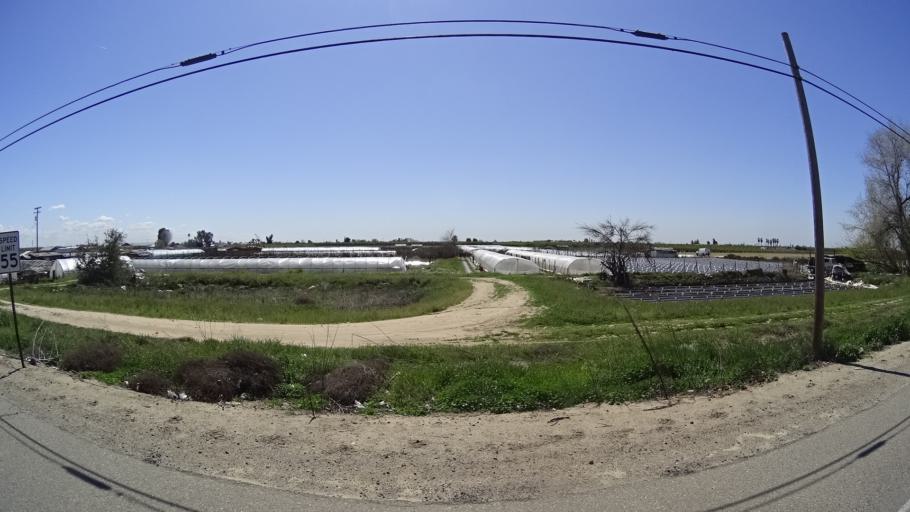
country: US
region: California
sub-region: Fresno County
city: West Park
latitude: 36.7066
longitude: -119.8483
